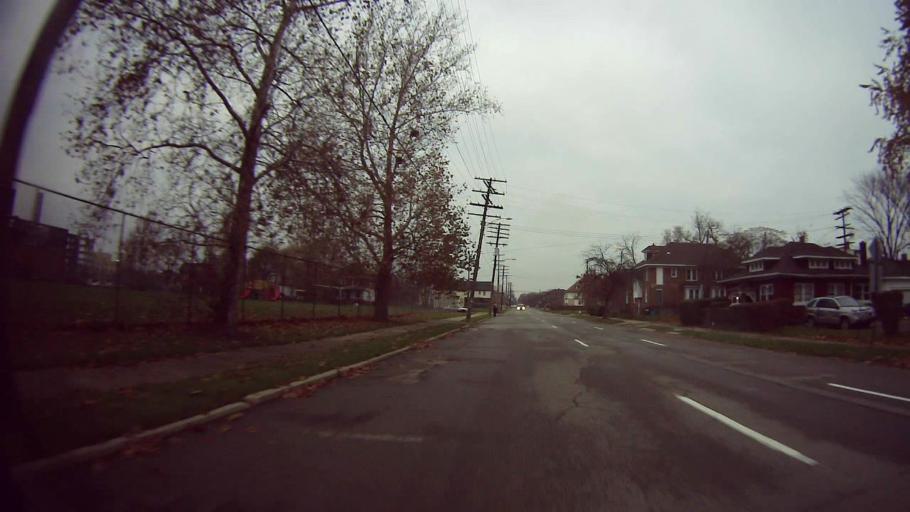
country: US
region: Michigan
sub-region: Wayne County
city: Highland Park
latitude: 42.3832
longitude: -83.0783
